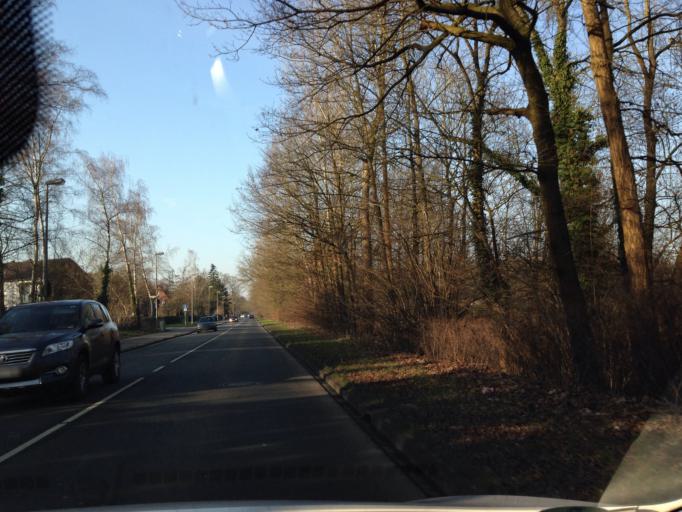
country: DE
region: North Rhine-Westphalia
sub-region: Regierungsbezirk Munster
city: Muenster
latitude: 51.9975
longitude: 7.6187
